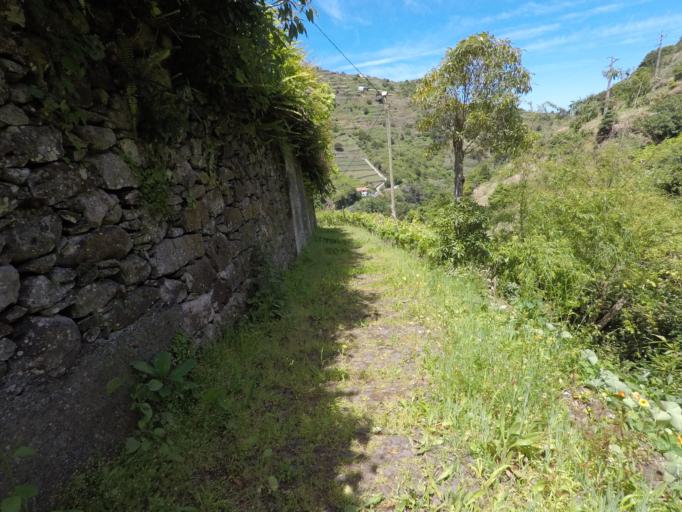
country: PT
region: Madeira
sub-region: Sao Vicente
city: Sao Vicente
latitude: 32.8212
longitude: -16.9741
